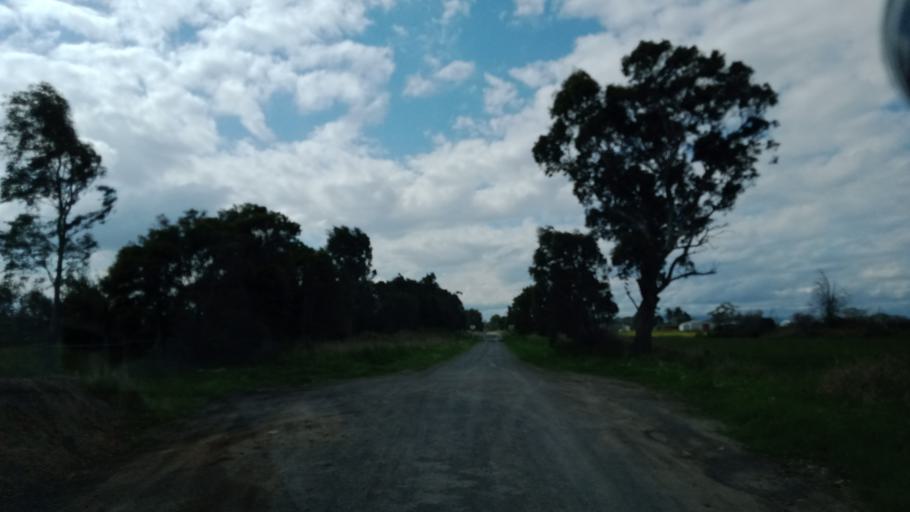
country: AU
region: Victoria
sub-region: Frankston
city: Sandhurst
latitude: -38.0831
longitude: 145.2199
